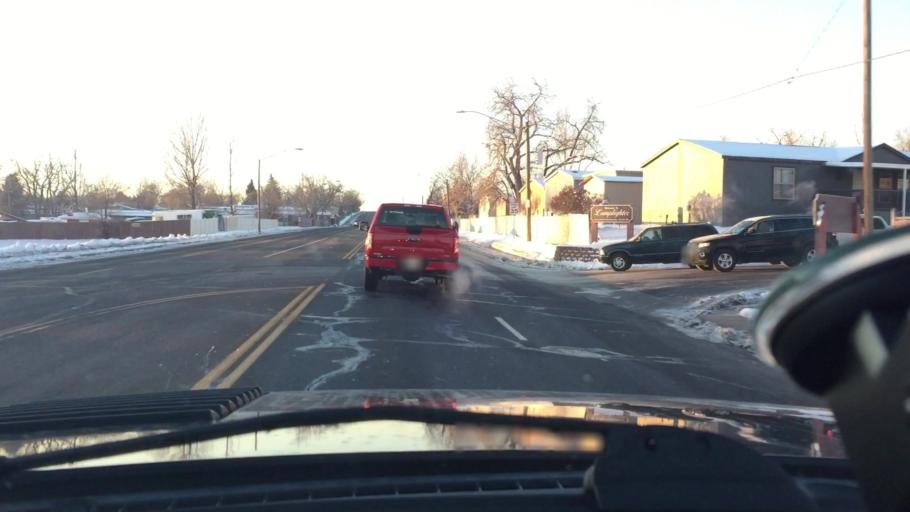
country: US
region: Colorado
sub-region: Adams County
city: Federal Heights
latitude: 39.8627
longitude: -105.0061
